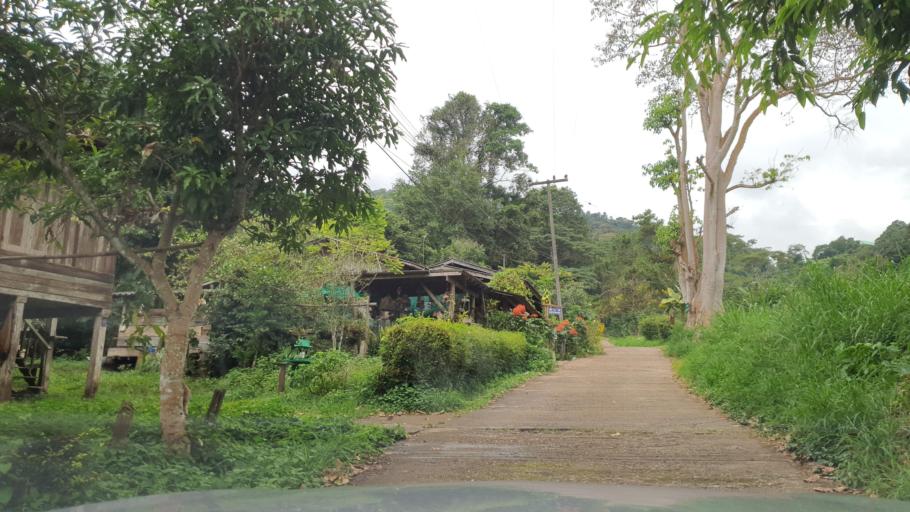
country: TH
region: Chiang Mai
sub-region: Amphoe Chiang Dao
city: Chiang Dao
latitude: 19.2512
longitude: 98.9226
